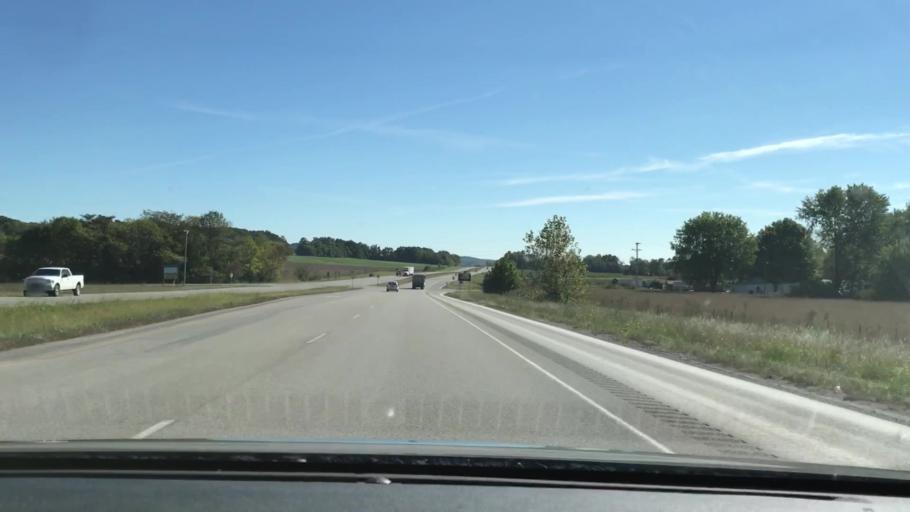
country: US
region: Kentucky
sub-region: Todd County
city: Elkton
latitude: 36.8471
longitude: -87.3033
